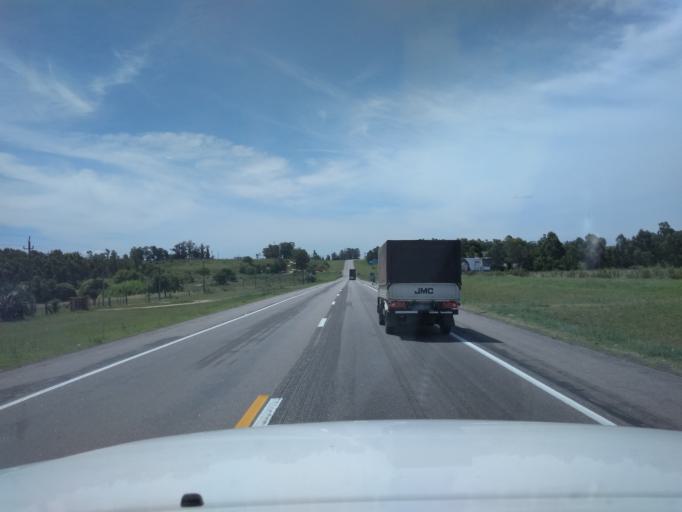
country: UY
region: Florida
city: Florida
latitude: -34.1289
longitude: -56.1865
